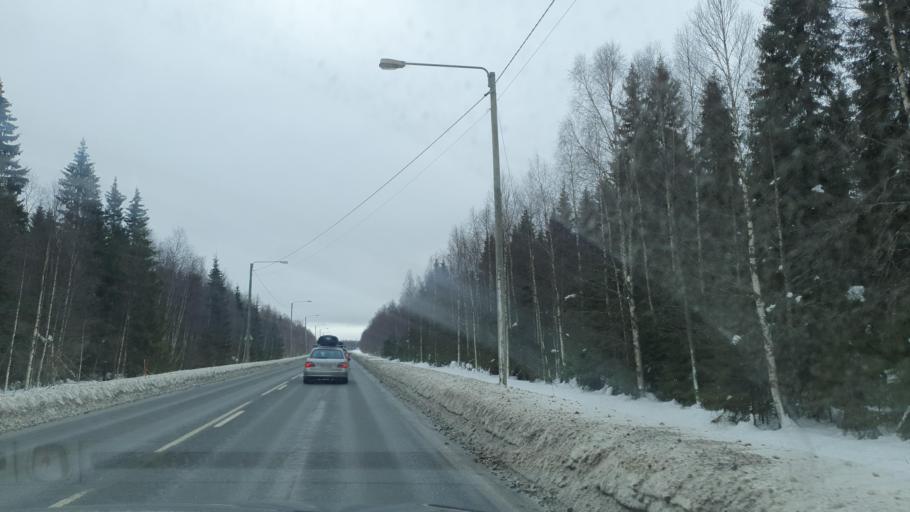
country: FI
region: Lapland
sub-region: Kemi-Tornio
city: Tornio
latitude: 66.0177
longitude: 24.0577
